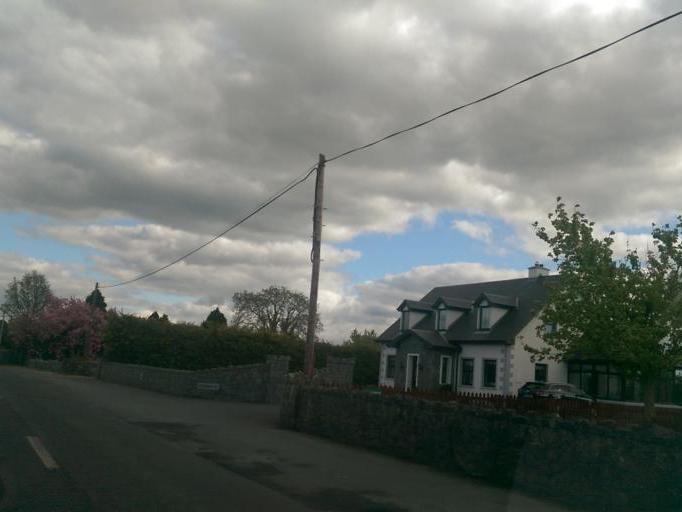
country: IE
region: Connaught
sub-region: County Galway
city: Ballinasloe
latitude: 53.3823
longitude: -8.2938
